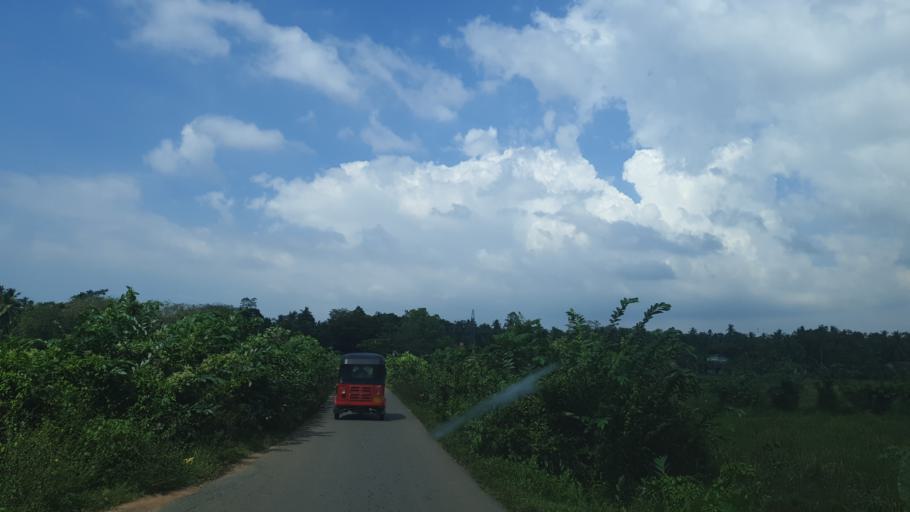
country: LK
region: Western
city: Horana South
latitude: 6.7016
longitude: 79.9859
